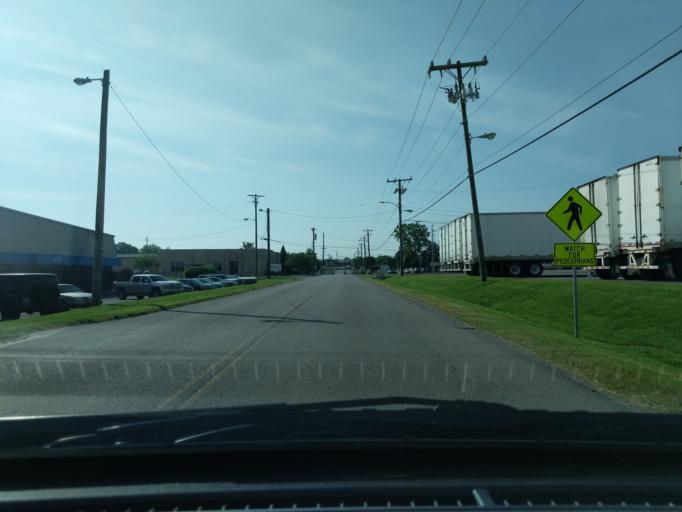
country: US
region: Tennessee
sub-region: Davidson County
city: Oak Hill
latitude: 36.0933
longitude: -86.6934
